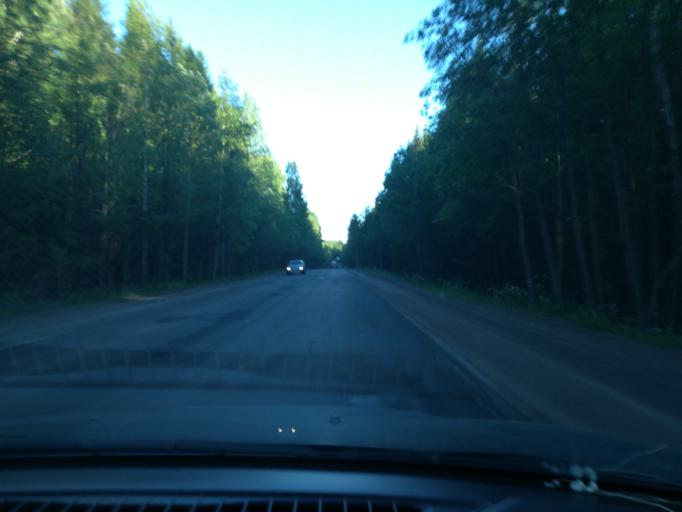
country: RU
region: Leningrad
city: Lesogorskiy
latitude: 60.9836
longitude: 28.9083
